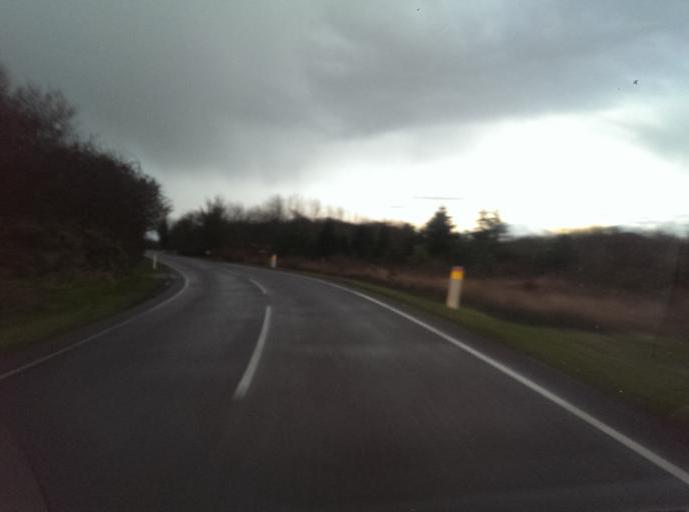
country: DK
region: South Denmark
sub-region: Esbjerg Kommune
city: Bramming
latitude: 55.4479
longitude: 8.6903
